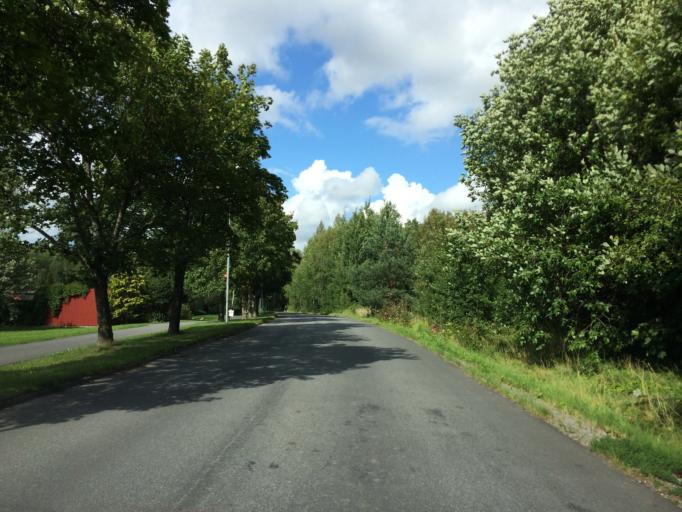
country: SE
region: Stockholm
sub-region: Upplands Vasby Kommun
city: Upplands Vaesby
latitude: 59.4643
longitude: 17.9096
